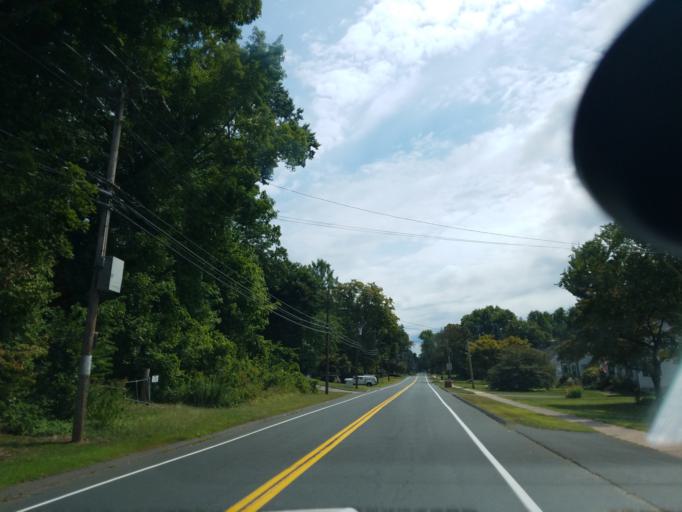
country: US
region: Connecticut
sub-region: Hartford County
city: Wethersfield
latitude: 41.6730
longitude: -72.6412
